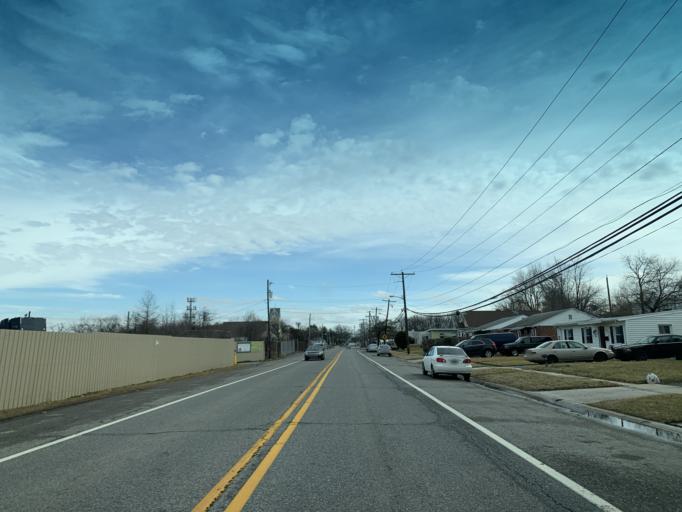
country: US
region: Delaware
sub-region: New Castle County
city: Wilmington
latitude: 39.7142
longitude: -75.5509
